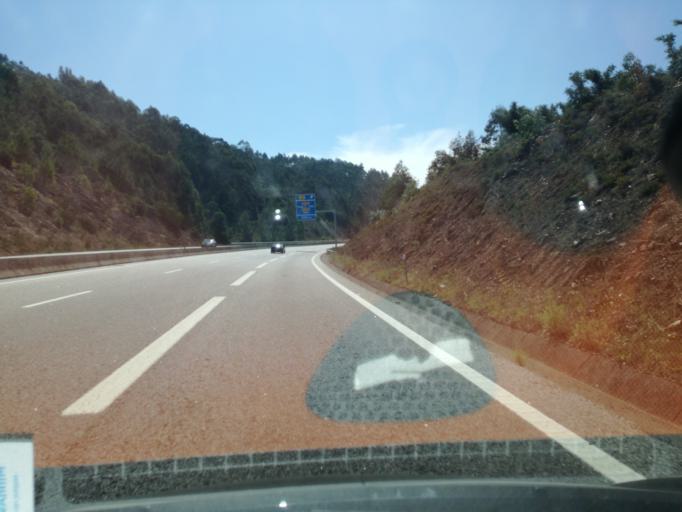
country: PT
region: Viana do Castelo
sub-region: Vila Nova de Cerveira
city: Vila Nova de Cerveira
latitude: 41.8674
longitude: -8.7816
